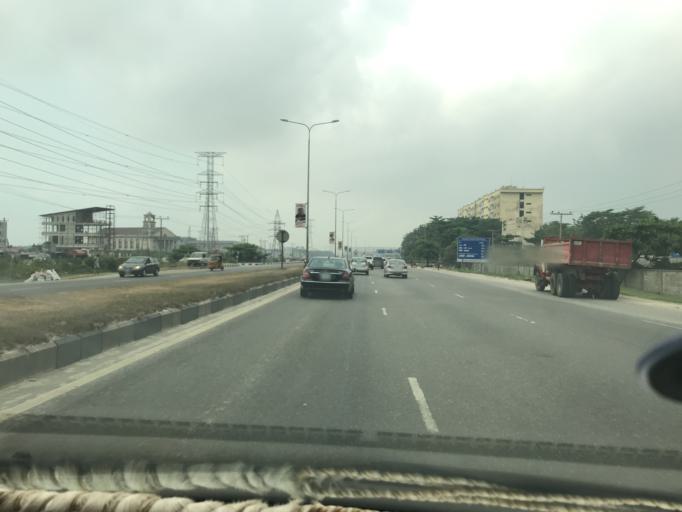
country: NG
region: Lagos
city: Ikoyi
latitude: 6.4476
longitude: 3.5461
